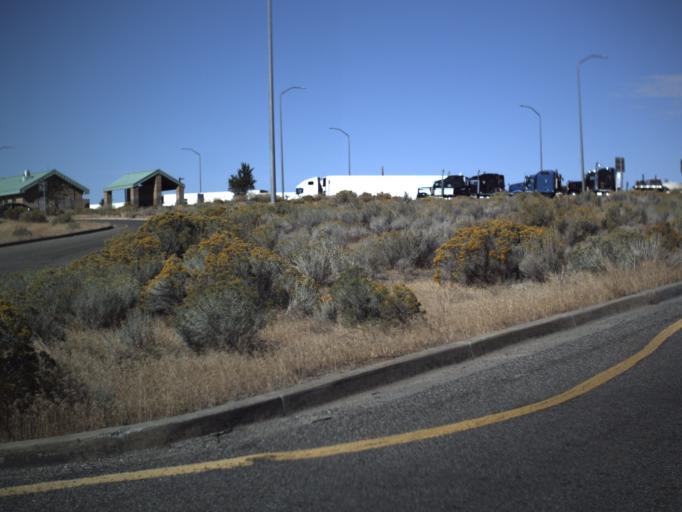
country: US
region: Utah
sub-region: Tooele County
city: Grantsville
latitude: 40.7623
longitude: -113.0084
